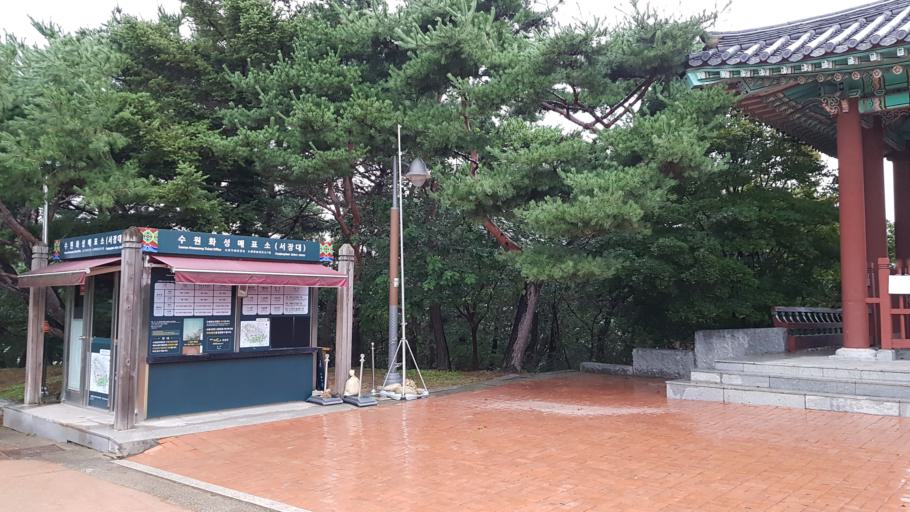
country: KR
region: Gyeonggi-do
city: Suwon-si
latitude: 37.2794
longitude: 127.0102
